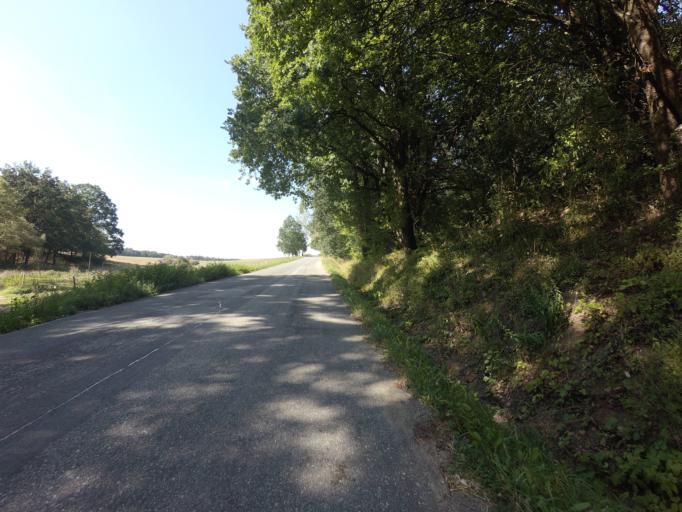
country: CZ
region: Jihocesky
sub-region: Okres Ceske Budejovice
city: Hluboka nad Vltavou
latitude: 49.1382
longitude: 14.4483
